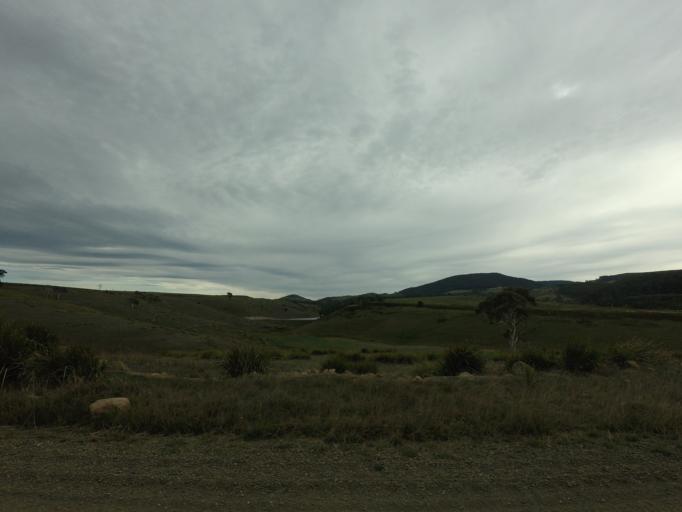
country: AU
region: Tasmania
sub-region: Derwent Valley
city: New Norfolk
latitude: -42.3956
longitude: 146.9136
